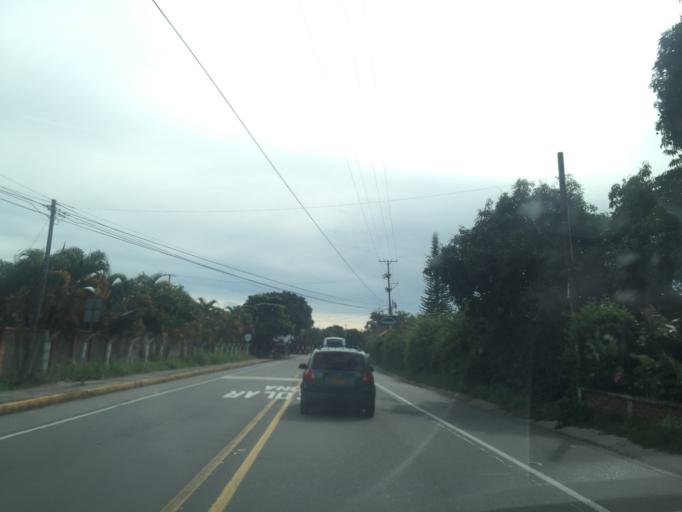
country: CO
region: Quindio
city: La Tebaida
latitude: 4.4869
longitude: -75.7451
